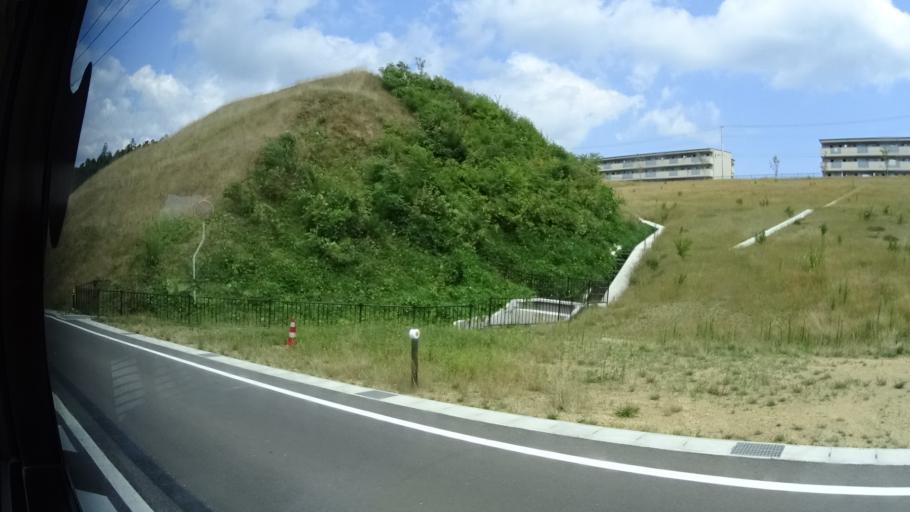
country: JP
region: Miyagi
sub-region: Oshika Gun
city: Onagawa Cho
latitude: 38.6800
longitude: 141.4591
